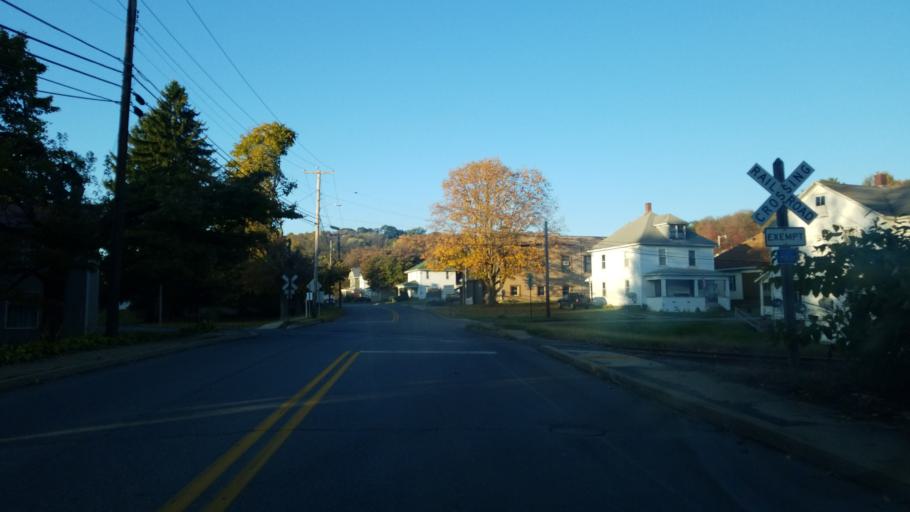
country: US
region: Pennsylvania
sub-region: Jefferson County
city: Punxsutawney
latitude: 40.9517
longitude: -78.9646
